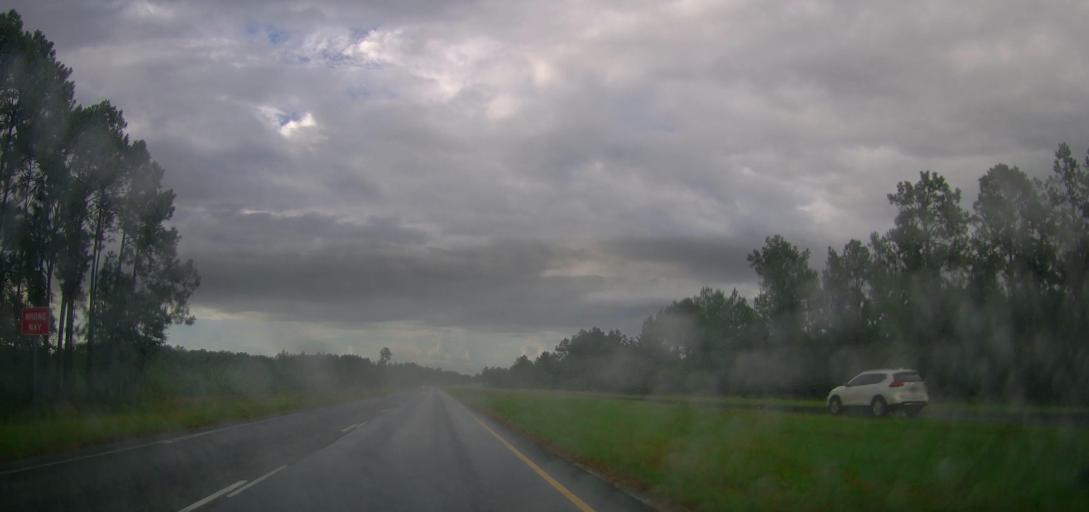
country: US
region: Georgia
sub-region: Ware County
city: Deenwood
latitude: 31.2236
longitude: -82.4247
